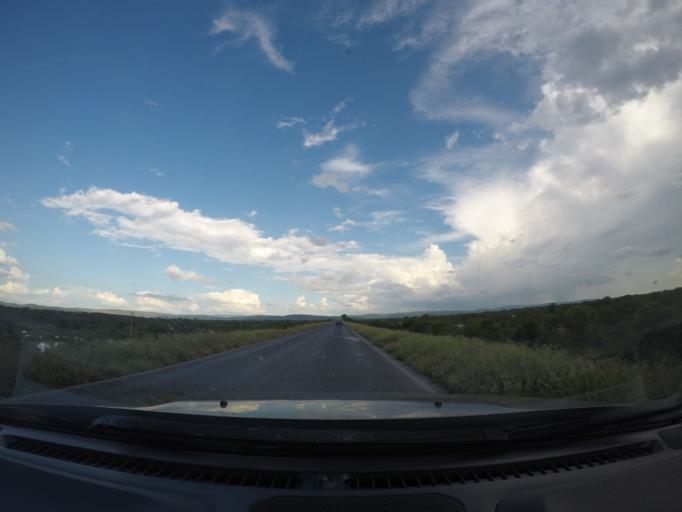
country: BR
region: Bahia
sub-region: Ibotirama
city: Ibotirama
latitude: -12.1690
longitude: -43.2692
